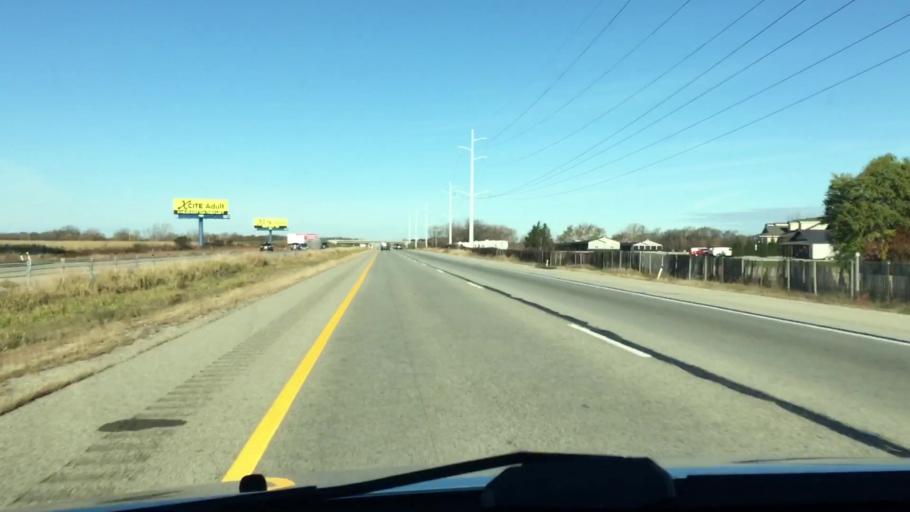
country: US
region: Wisconsin
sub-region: Fond du Lac County
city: North Fond du Lac
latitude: 43.8174
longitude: -88.5172
